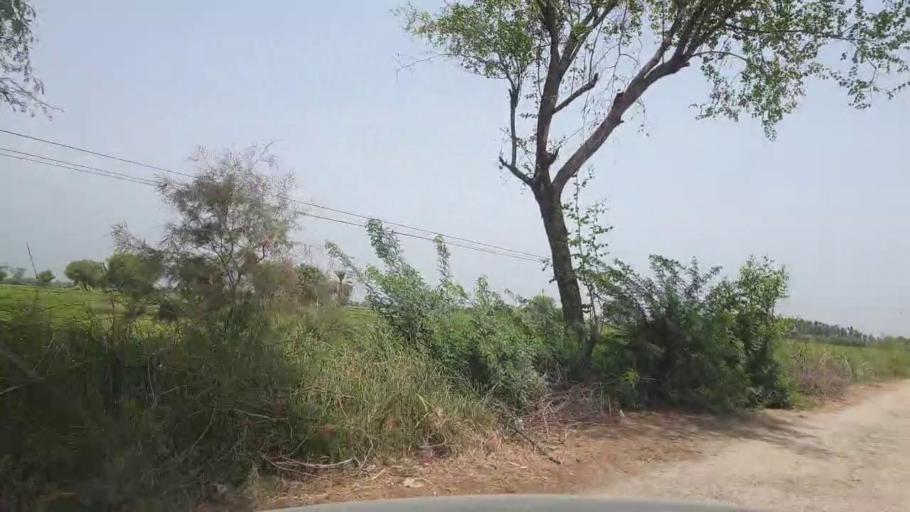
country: PK
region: Sindh
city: Garhi Yasin
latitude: 27.9224
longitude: 68.3751
